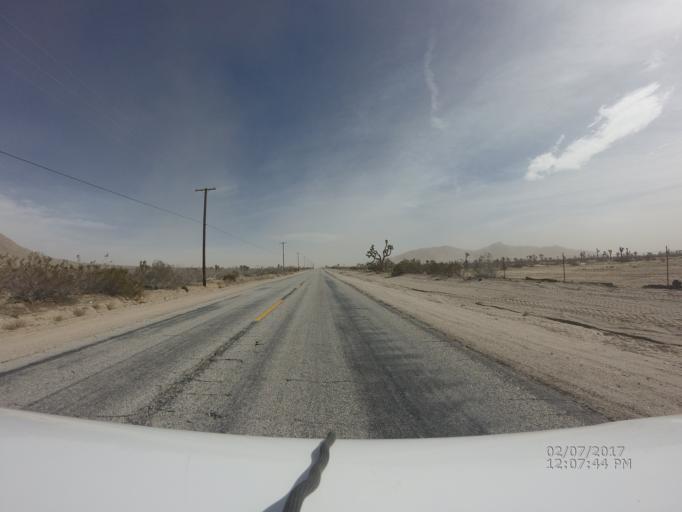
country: US
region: California
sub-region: Los Angeles County
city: Lake Los Angeles
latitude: 34.6899
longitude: -117.8332
